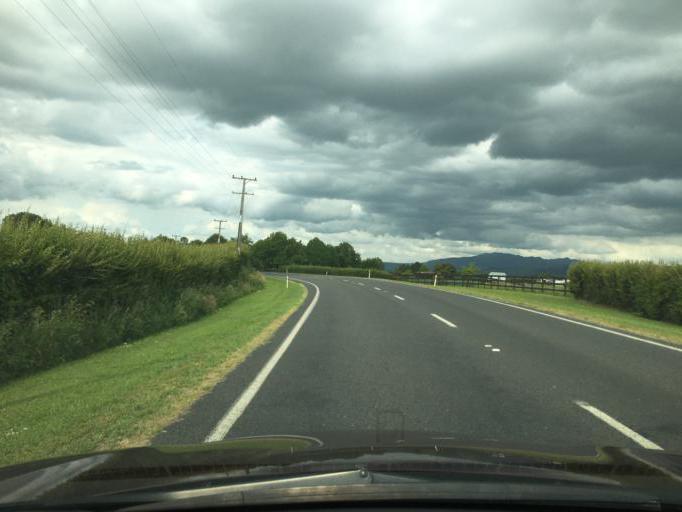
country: NZ
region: Waikato
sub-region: Waipa District
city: Cambridge
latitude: -38.0025
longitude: 175.3886
